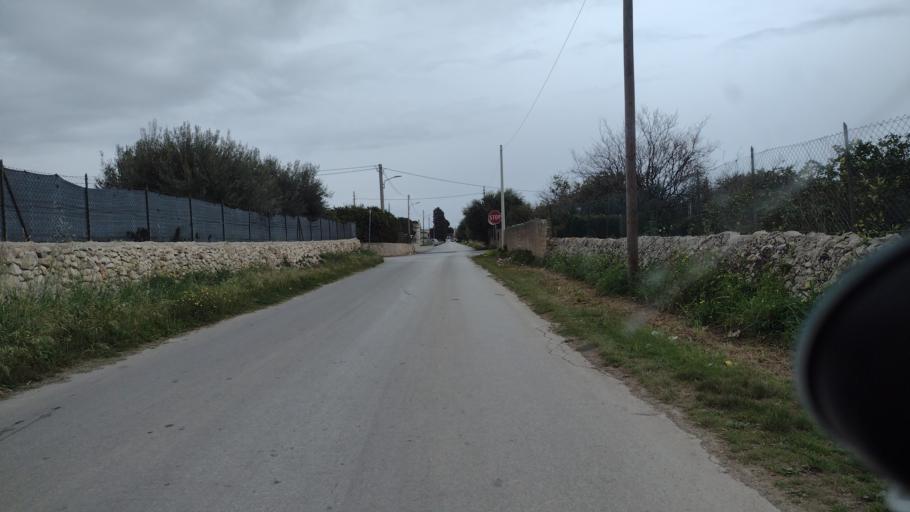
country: IT
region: Sicily
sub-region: Provincia di Siracusa
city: Avola
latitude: 36.9111
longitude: 15.1220
